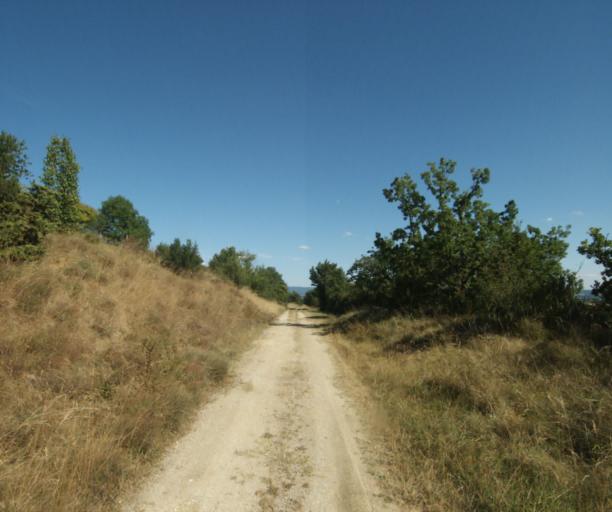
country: FR
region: Midi-Pyrenees
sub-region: Departement de la Haute-Garonne
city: Saint-Felix-Lauragais
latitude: 43.5150
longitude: 1.9223
